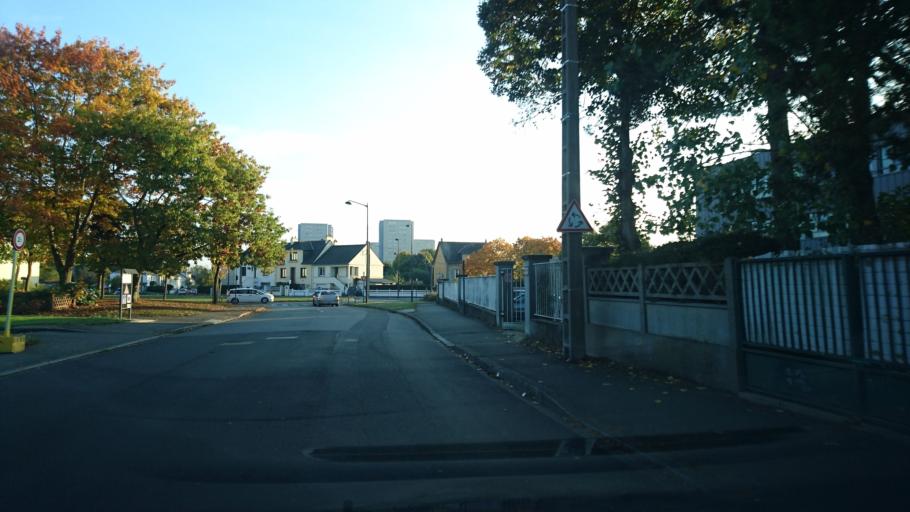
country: FR
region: Brittany
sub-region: Departement d'Ille-et-Vilaine
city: Rennes
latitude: 48.0922
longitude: -1.6617
